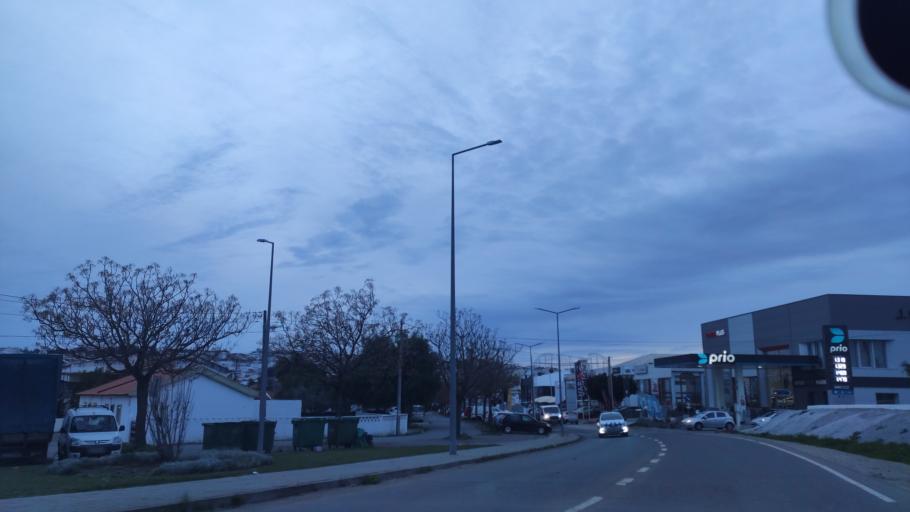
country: PT
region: Beja
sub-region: Beja
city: Beja
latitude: 38.0201
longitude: -7.8483
